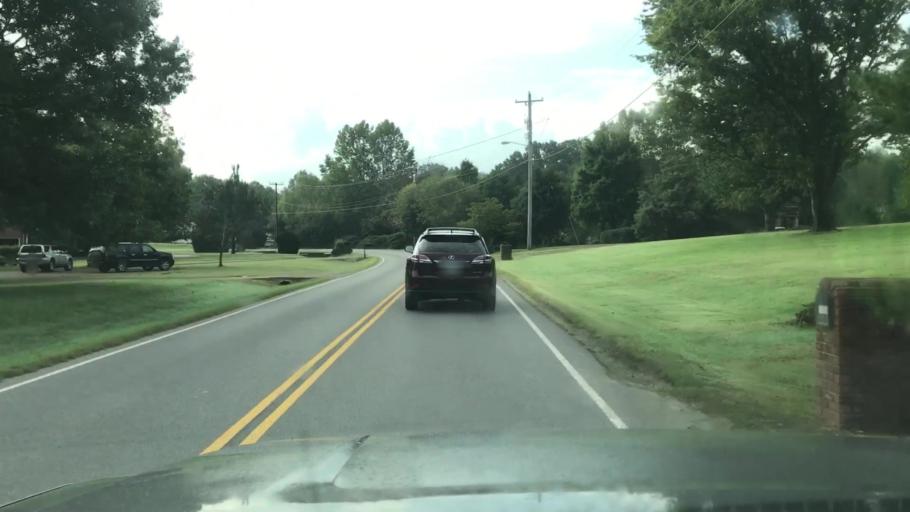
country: US
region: Tennessee
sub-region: Davidson County
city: Forest Hills
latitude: 36.0274
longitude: -86.8291
